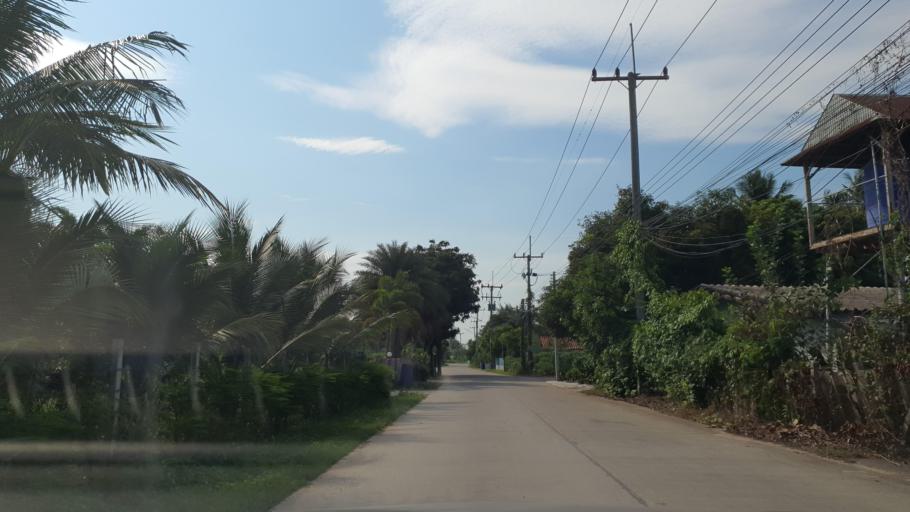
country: TH
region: Chon Buri
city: Sattahip
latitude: 12.7902
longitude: 100.9418
